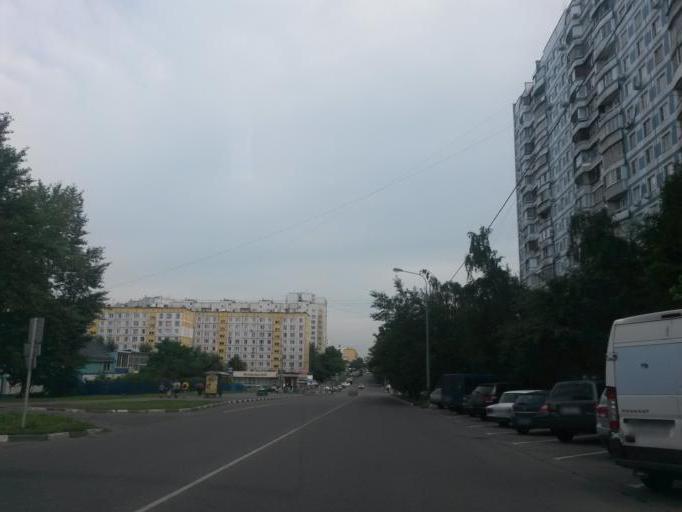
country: RU
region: Moscow
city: Orekhovo-Borisovo
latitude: 55.6115
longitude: 37.7311
